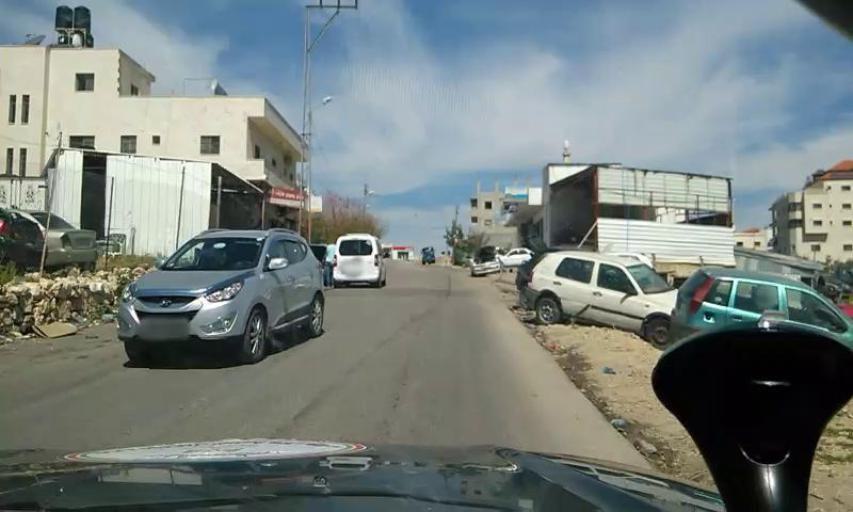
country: PS
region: West Bank
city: Bayt `Ur at Tahta
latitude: 31.8933
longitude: 35.0888
